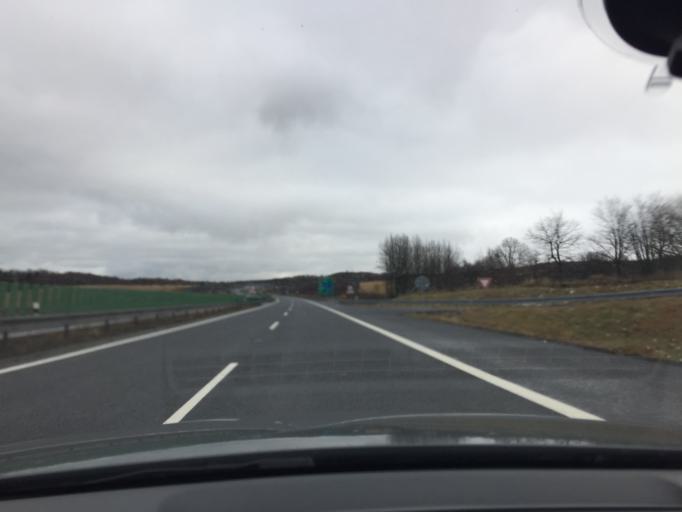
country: CZ
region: Ustecky
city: Chlumec
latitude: 50.7721
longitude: 13.9529
